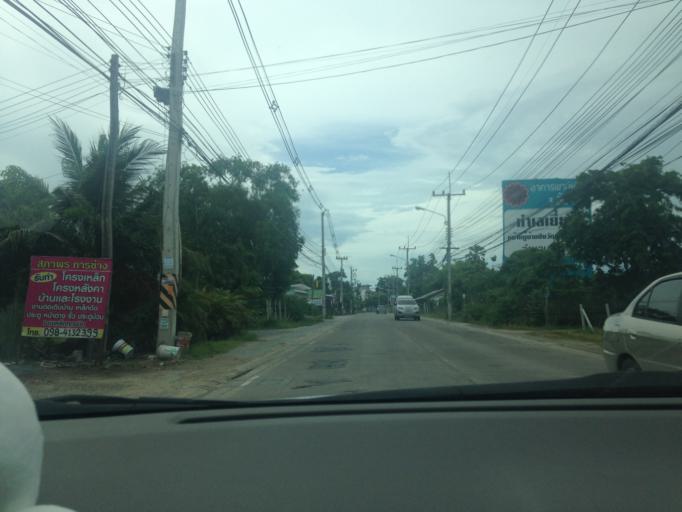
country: TH
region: Chon Buri
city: Chon Buri
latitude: 13.3236
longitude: 100.9279
